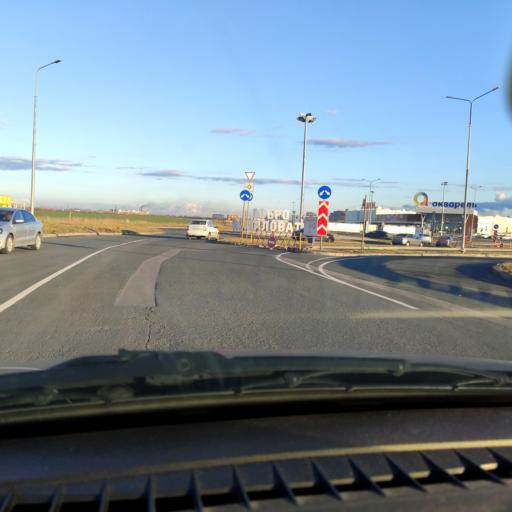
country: RU
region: Samara
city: Tol'yatti
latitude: 53.5529
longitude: 49.3418
